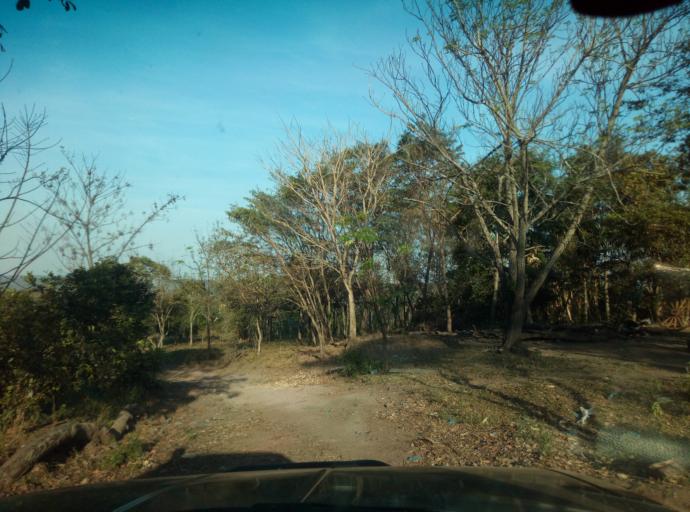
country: PY
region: Caaguazu
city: Doctor Cecilio Baez
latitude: -25.2005
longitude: -56.1300
